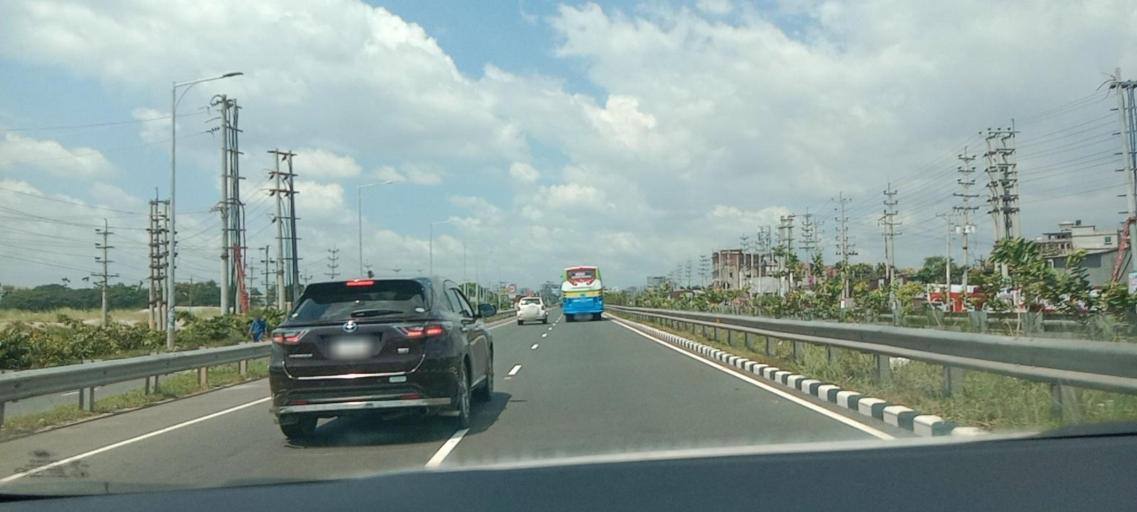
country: BD
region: Dhaka
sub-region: Dhaka
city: Dhaka
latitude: 23.6775
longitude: 90.4084
